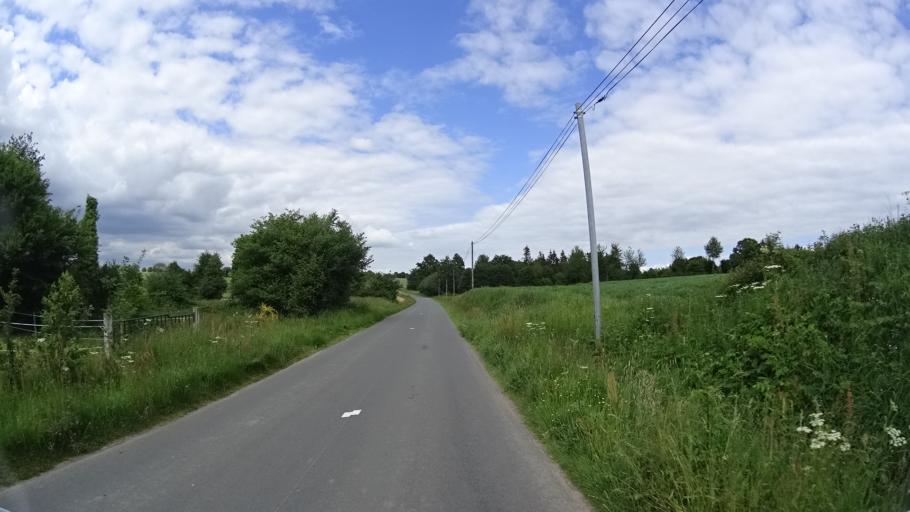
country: FR
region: Brittany
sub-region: Departement d'Ille-et-Vilaine
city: Plelan-le-Grand
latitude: 48.0820
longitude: -2.1018
